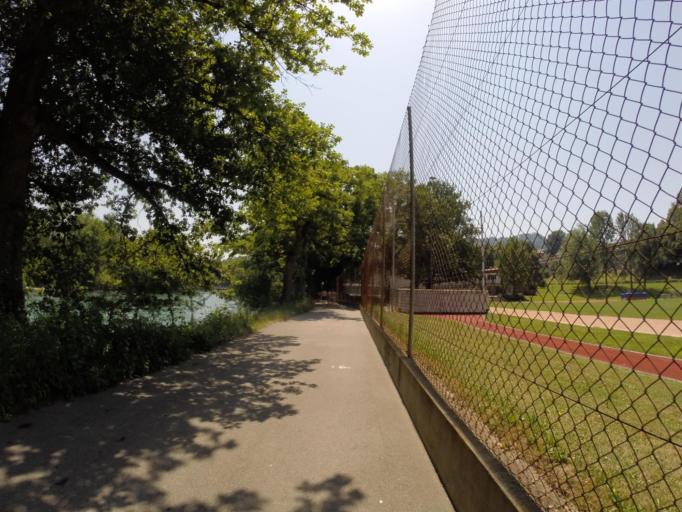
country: CH
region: Bern
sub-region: Bern-Mittelland District
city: Bern
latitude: 46.9359
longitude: 7.4444
